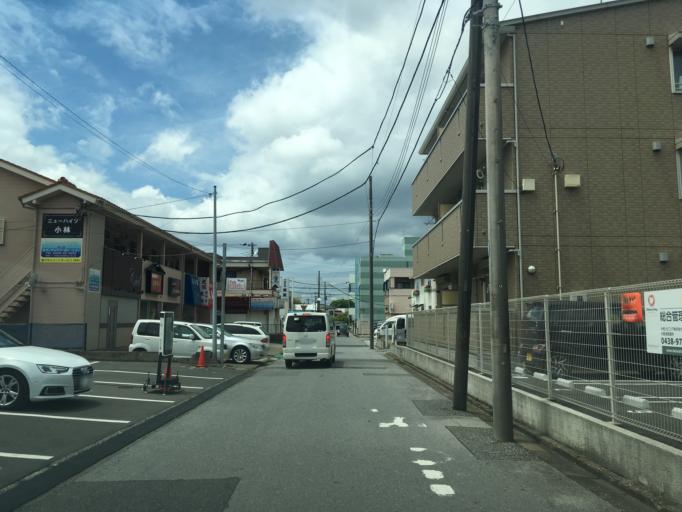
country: JP
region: Chiba
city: Kimitsu
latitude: 35.3313
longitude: 139.8994
